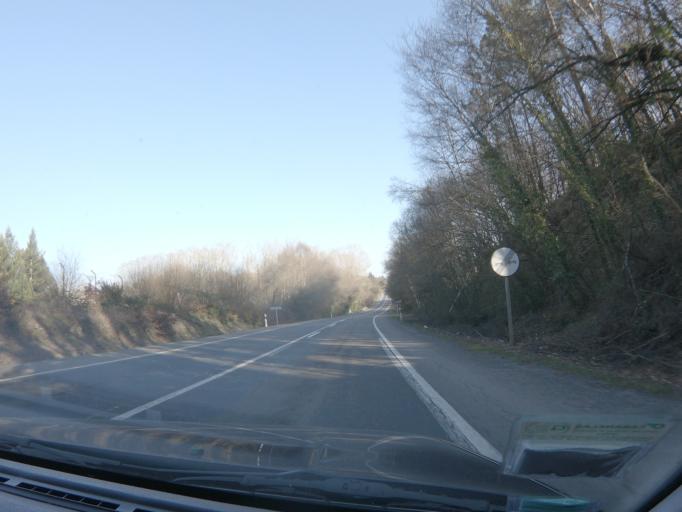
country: ES
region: Galicia
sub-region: Provincia de Lugo
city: Corgo
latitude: 42.9628
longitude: -7.4823
